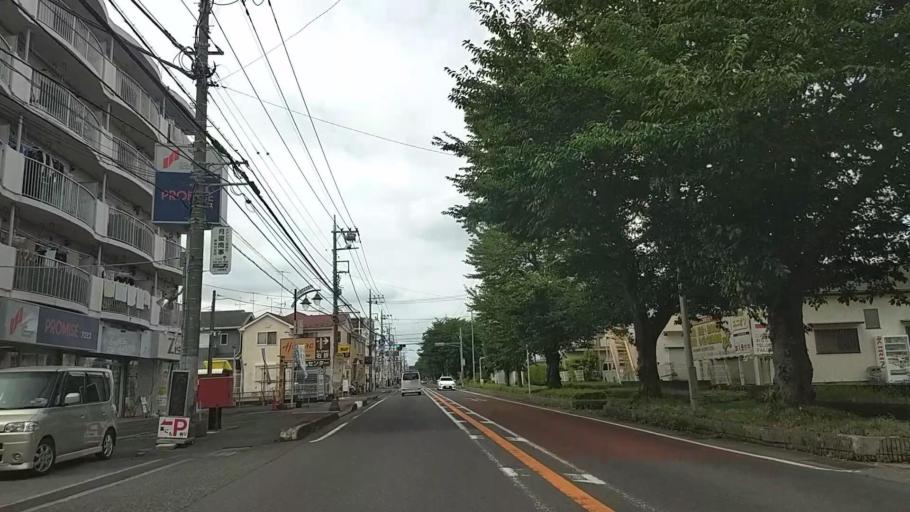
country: JP
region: Kanagawa
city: Minami-rinkan
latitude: 35.4433
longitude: 139.4672
